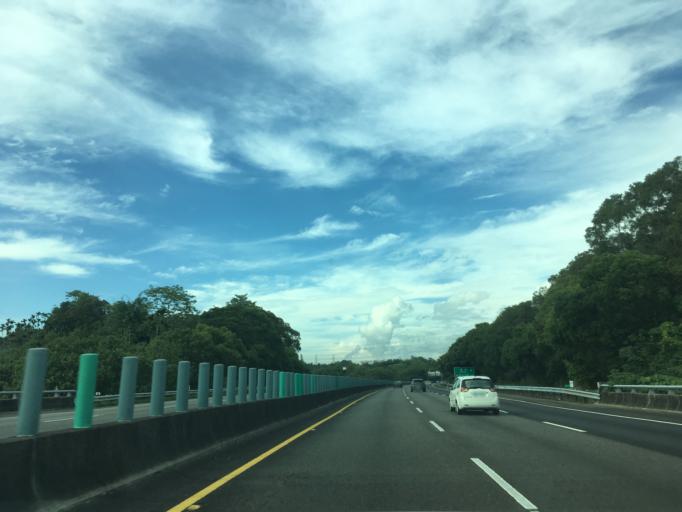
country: TW
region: Taiwan
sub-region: Chiayi
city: Jiayi Shi
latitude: 23.5352
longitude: 120.4913
